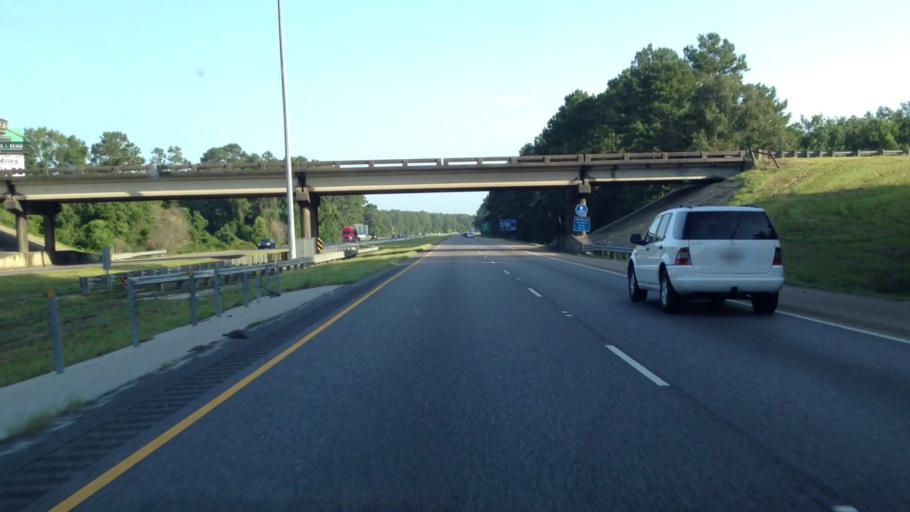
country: US
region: Louisiana
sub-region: Tangipahoa Parish
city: Hammond
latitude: 30.4908
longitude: -90.4974
